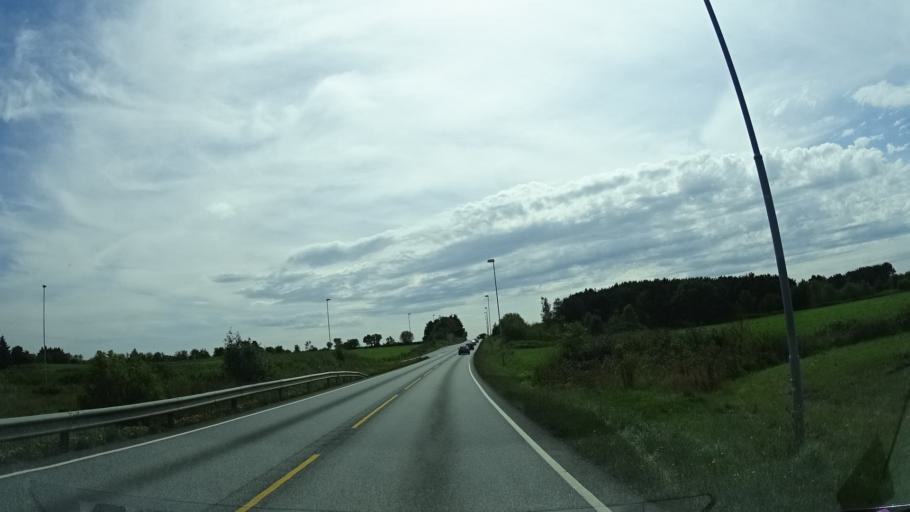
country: NO
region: Rogaland
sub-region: Randaberg
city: Randaberg
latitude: 59.0057
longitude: 5.6422
